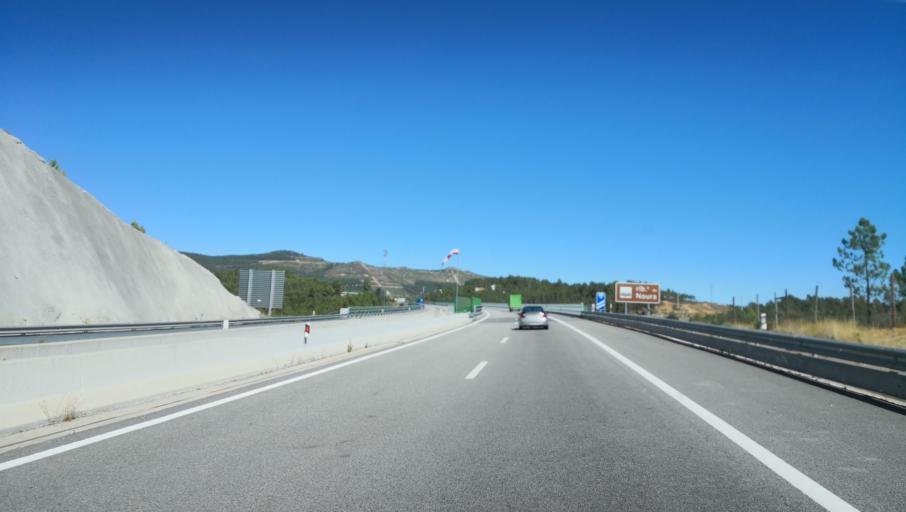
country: PT
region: Vila Real
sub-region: Murca
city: Murca
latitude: 41.4103
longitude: -7.4170
